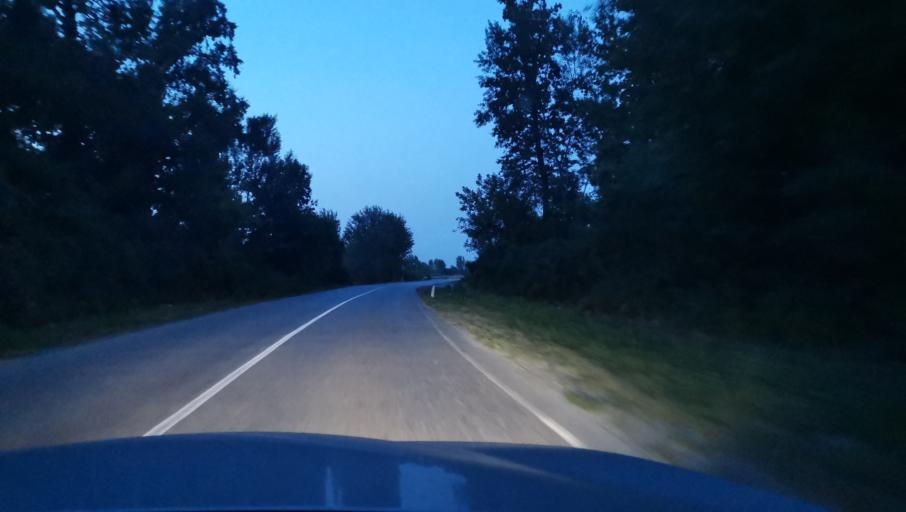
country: RS
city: Boljevci
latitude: 44.7105
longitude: 20.2073
